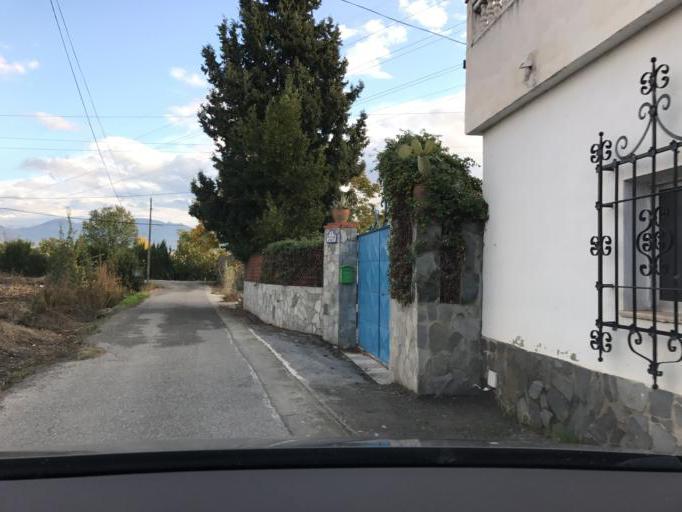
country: ES
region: Andalusia
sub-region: Provincia de Granada
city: Granada
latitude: 37.1773
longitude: -3.6241
